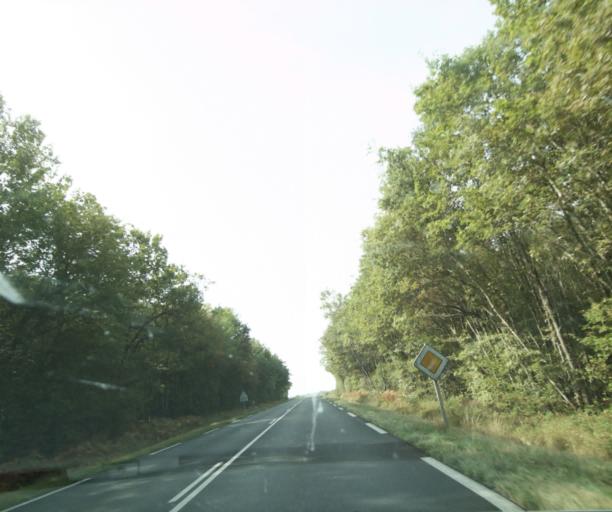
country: FR
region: Auvergne
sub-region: Departement de l'Allier
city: Saint-Francois
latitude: 46.4392
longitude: 3.9096
